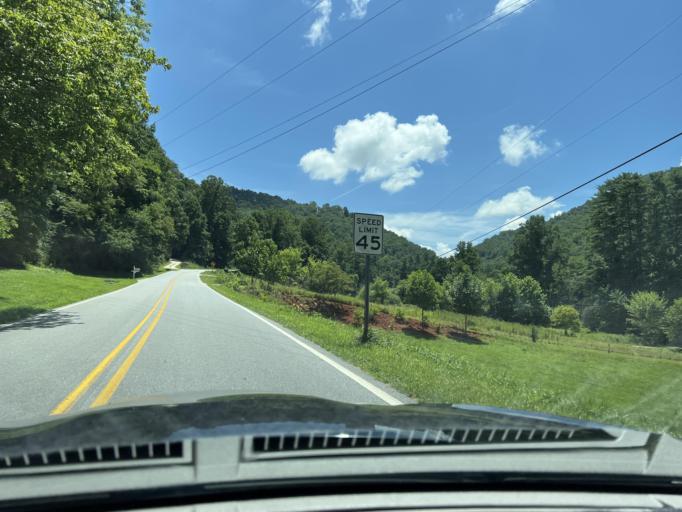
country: US
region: North Carolina
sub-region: Henderson County
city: Fruitland
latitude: 35.4285
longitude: -82.4236
